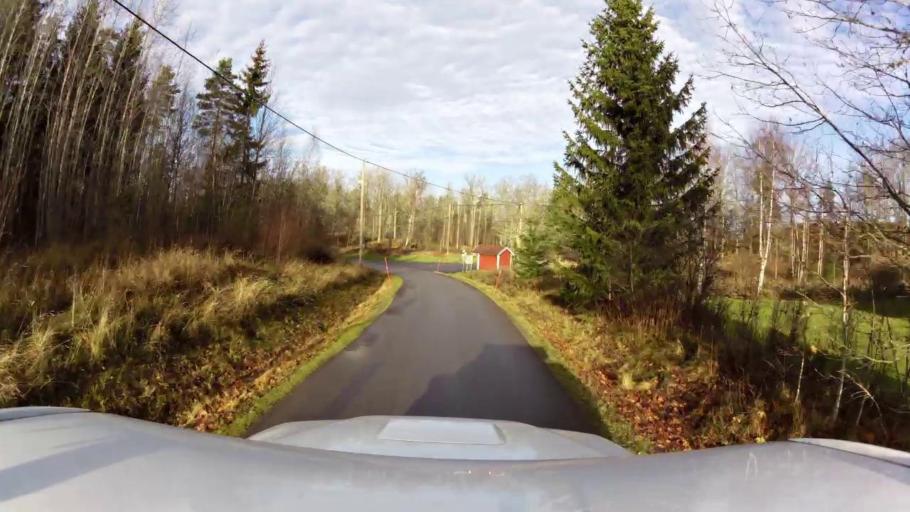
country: SE
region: OEstergoetland
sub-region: Linkopings Kommun
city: Sturefors
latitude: 58.2584
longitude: 15.6954
